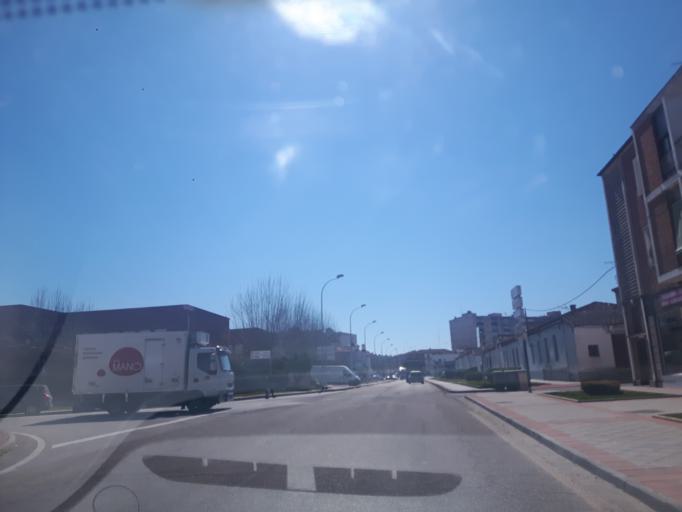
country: ES
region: Castille and Leon
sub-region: Provincia de Salamanca
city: Penaranda de Bracamonte
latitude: 40.9023
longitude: -5.2052
